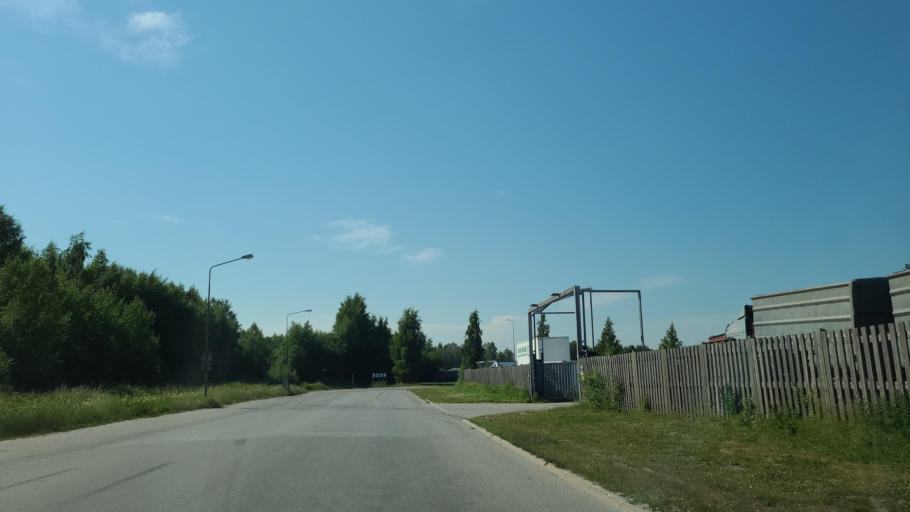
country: SE
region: Vaesterbotten
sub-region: Umea Kommun
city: Roback
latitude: 63.8445
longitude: 20.2132
